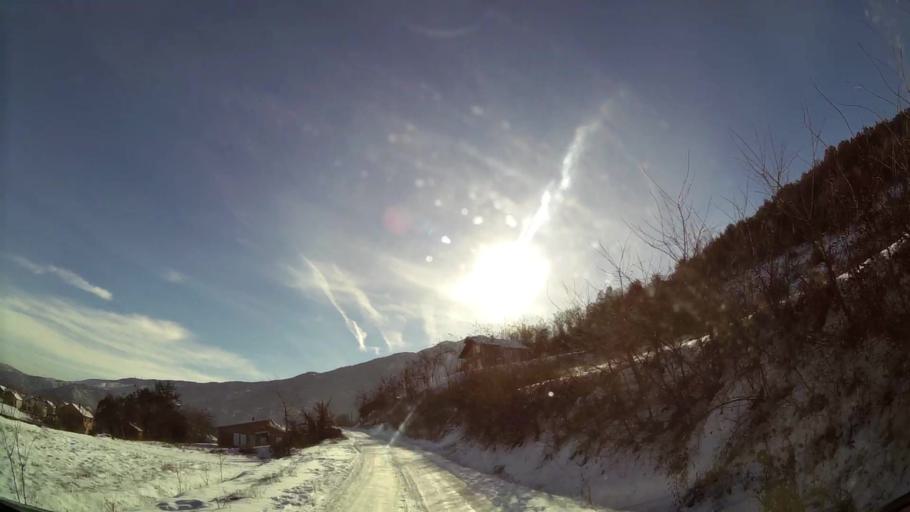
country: MK
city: Ljubin
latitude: 41.9814
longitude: 21.3006
